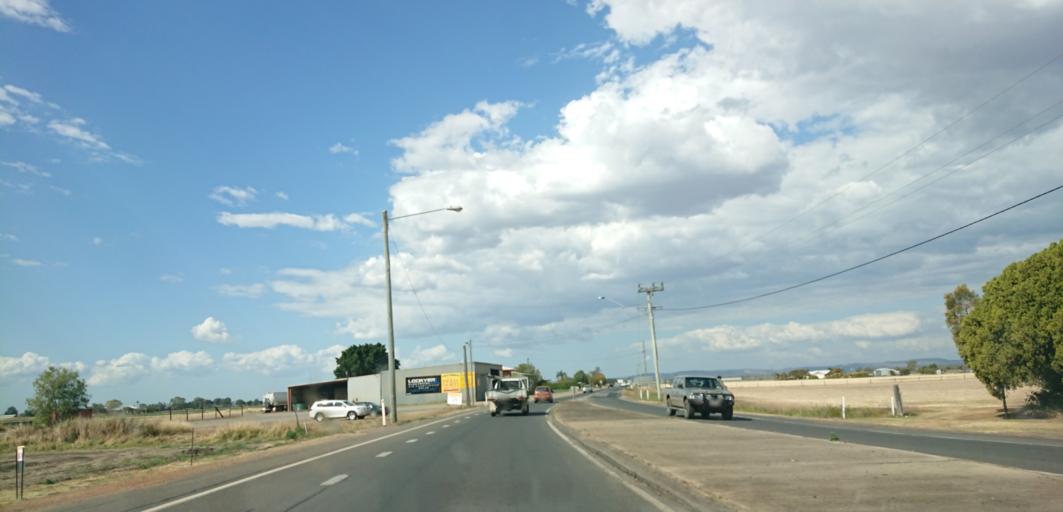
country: AU
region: Queensland
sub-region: Lockyer Valley
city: Gatton
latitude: -27.5547
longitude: 152.2900
